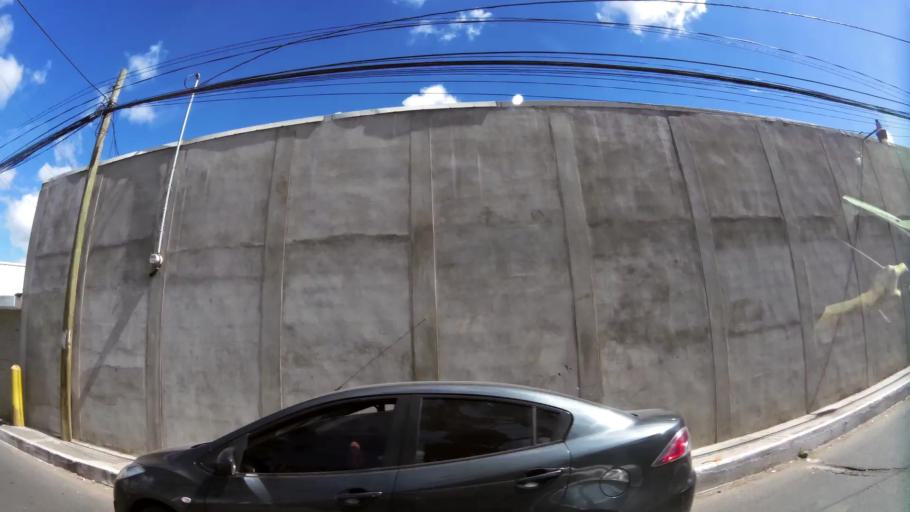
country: GT
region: Guatemala
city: Petapa
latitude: 14.5510
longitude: -90.5436
